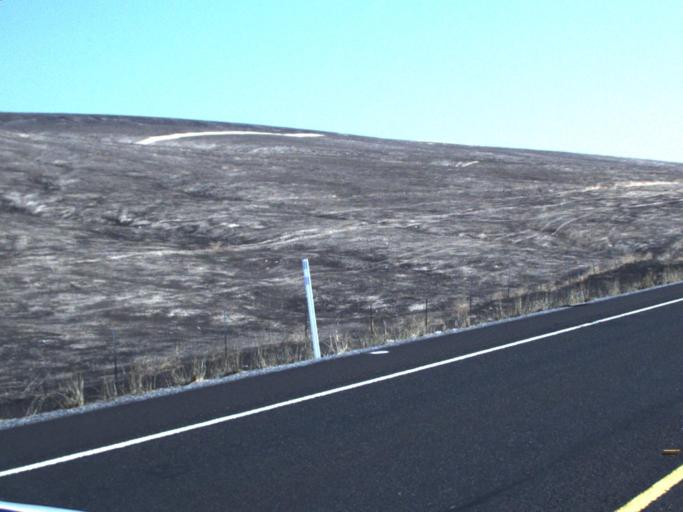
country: US
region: Washington
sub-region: Grant County
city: Desert Aire
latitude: 46.5421
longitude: -119.8474
